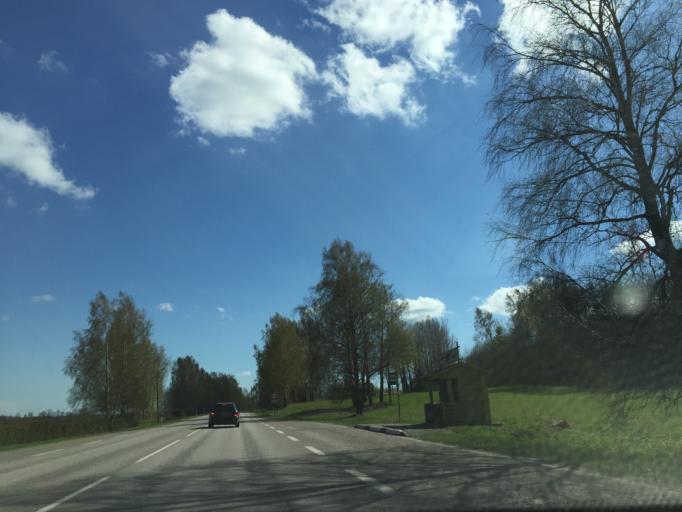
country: EE
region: Valgamaa
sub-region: Valga linn
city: Valga
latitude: 57.8894
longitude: 26.0565
